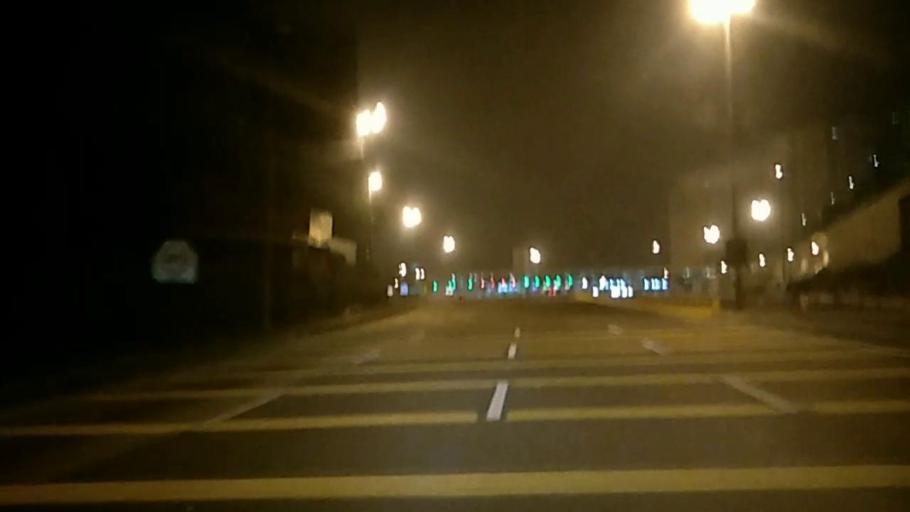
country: MY
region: Selangor
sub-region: Petaling
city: Petaling Jaya
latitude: 3.1811
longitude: 101.6192
